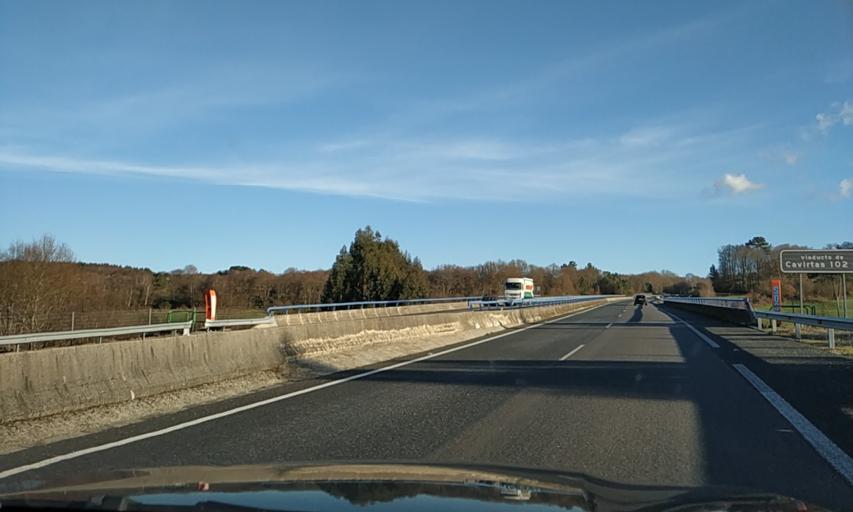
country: ES
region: Galicia
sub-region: Provincia de Pontevedra
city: Lalin
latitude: 42.6619
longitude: -8.1451
